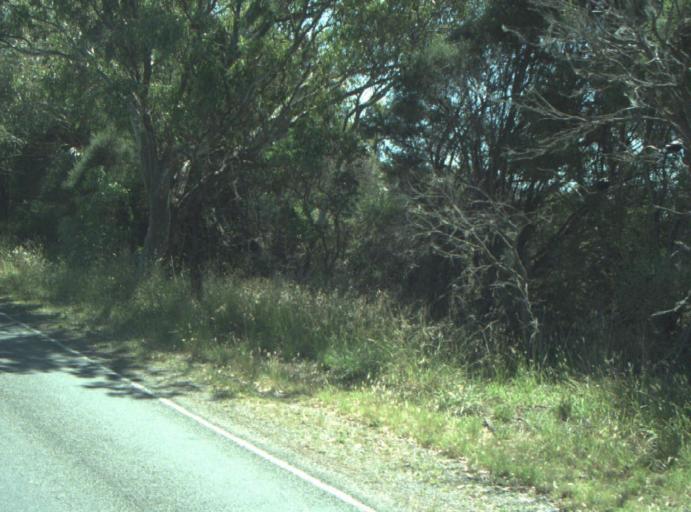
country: AU
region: Victoria
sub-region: Greater Geelong
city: Breakwater
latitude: -38.2123
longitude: 144.3582
